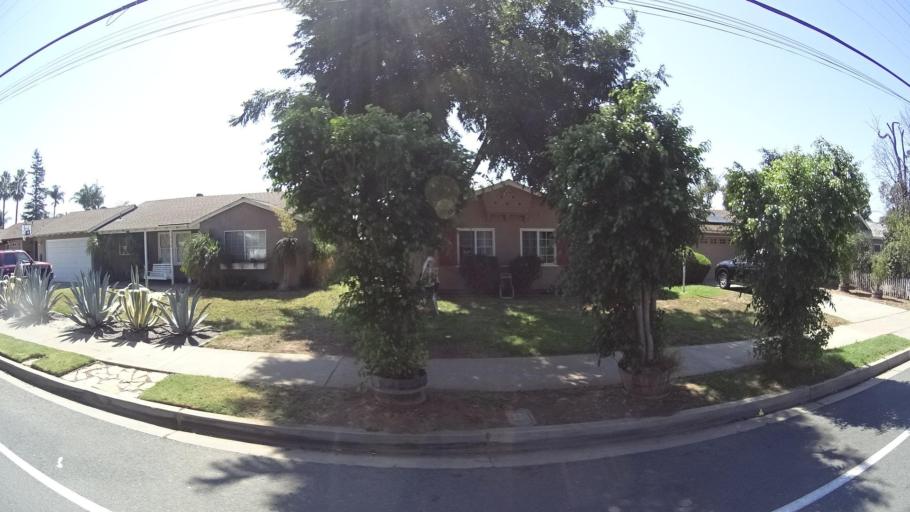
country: US
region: California
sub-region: San Diego County
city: Bostonia
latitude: 32.8002
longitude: -116.9252
